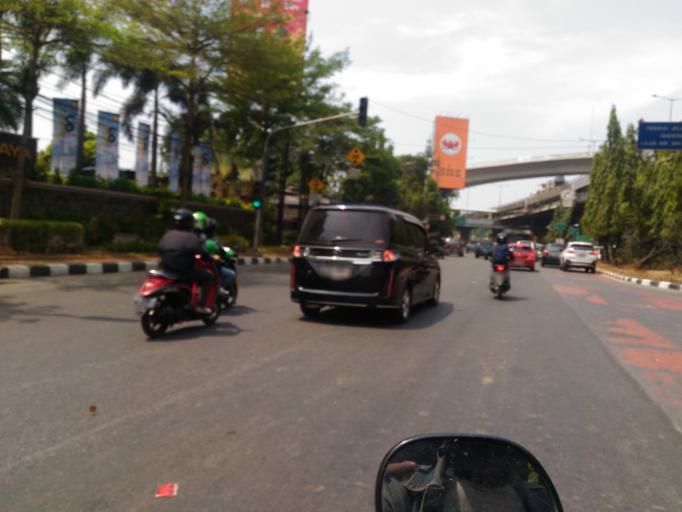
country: ID
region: Jakarta Raya
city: Jakarta
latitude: -6.2405
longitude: 106.8775
